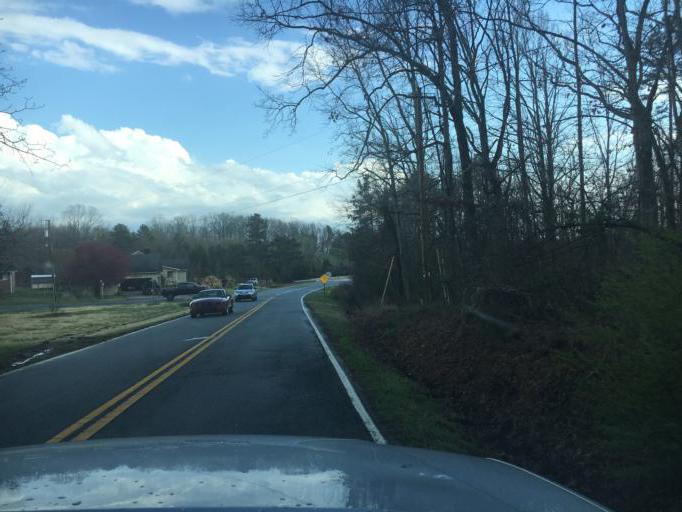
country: US
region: South Carolina
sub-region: Greenville County
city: Parker
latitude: 34.8504
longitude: -82.4947
